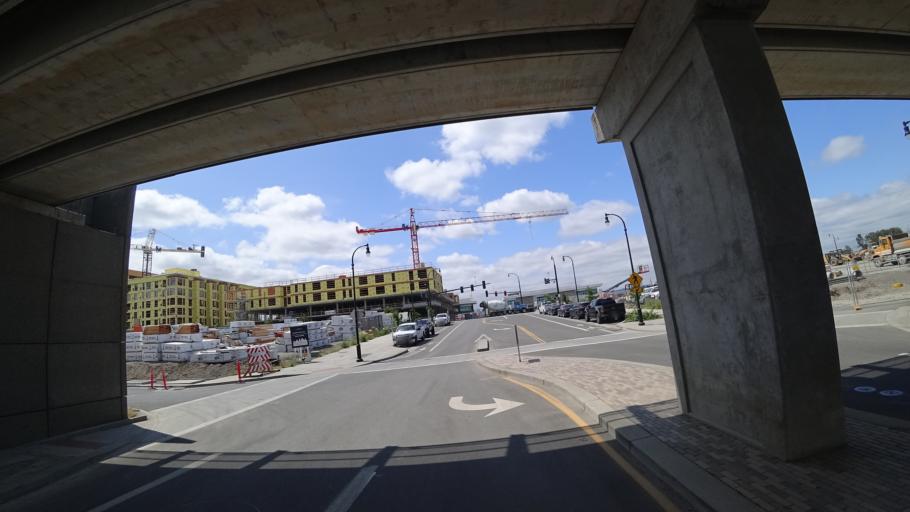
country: US
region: Washington
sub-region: Clark County
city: Vancouver
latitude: 45.6256
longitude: -122.6792
